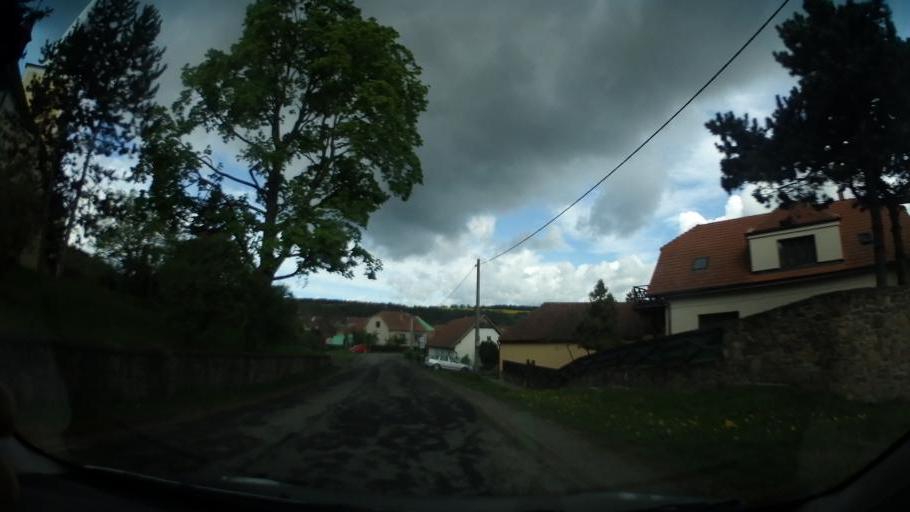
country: CZ
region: South Moravian
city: Ricany
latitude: 49.2353
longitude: 16.4052
